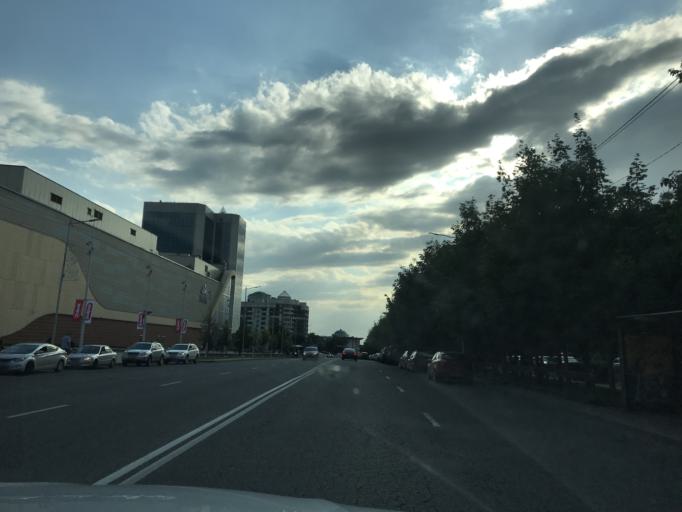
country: KZ
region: Almaty Qalasy
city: Almaty
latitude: 43.2343
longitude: 76.9573
